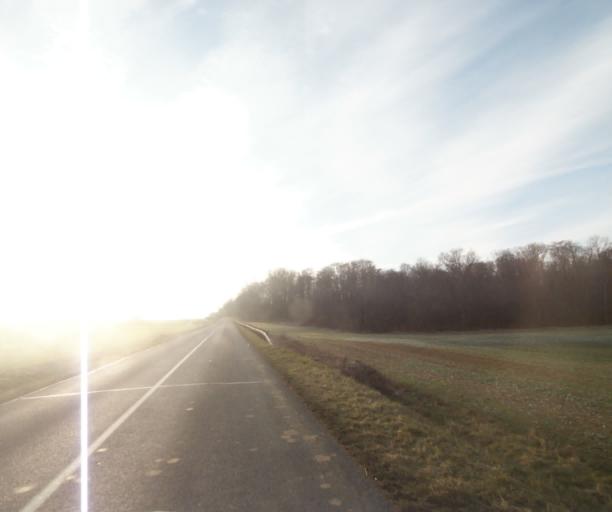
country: FR
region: Champagne-Ardenne
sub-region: Departement de la Haute-Marne
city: Chancenay
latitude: 48.7197
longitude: 4.9429
